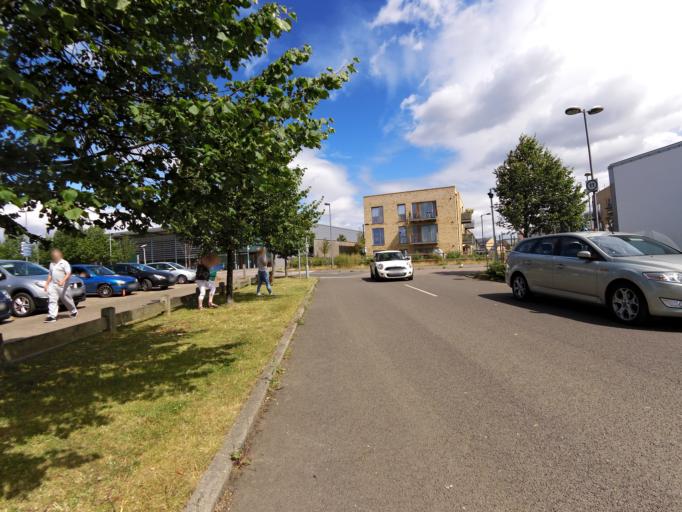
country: GB
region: England
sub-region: Cambridgeshire
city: Grantchester
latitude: 52.1687
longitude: 0.1083
